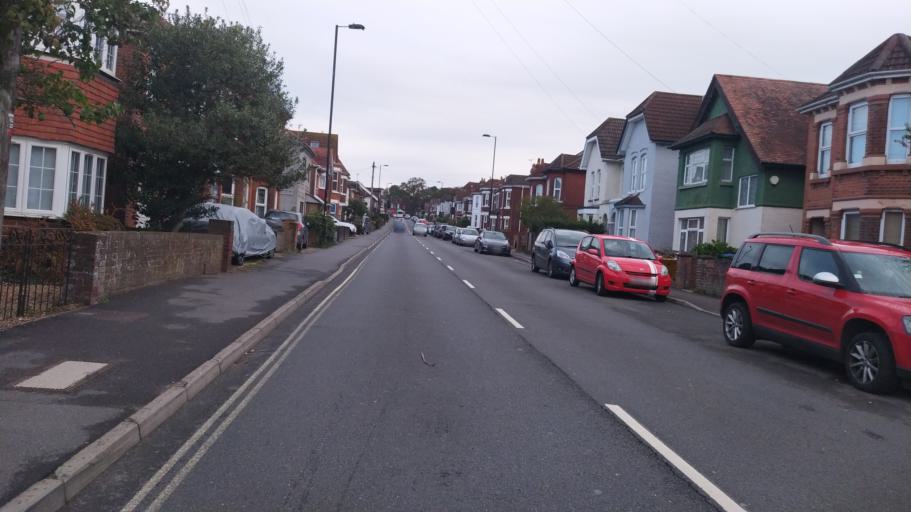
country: GB
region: England
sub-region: Southampton
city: Southampton
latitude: 50.9199
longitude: -1.3747
